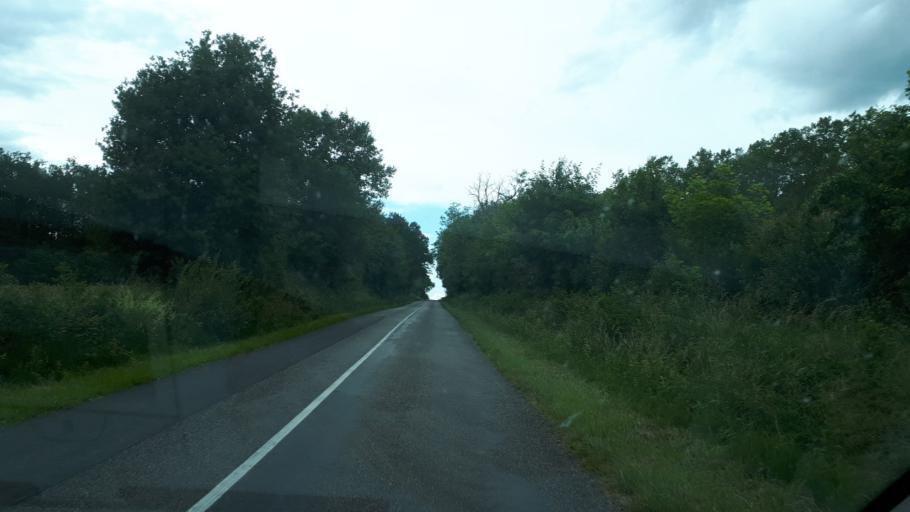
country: FR
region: Centre
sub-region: Departement du Cher
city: Gracay
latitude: 47.1992
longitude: 1.7766
